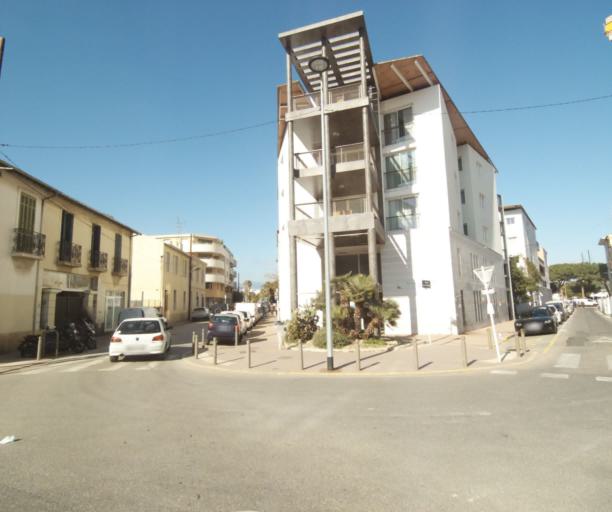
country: FR
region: Provence-Alpes-Cote d'Azur
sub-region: Departement des Alpes-Maritimes
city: Antibes
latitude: 43.5830
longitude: 7.1231
